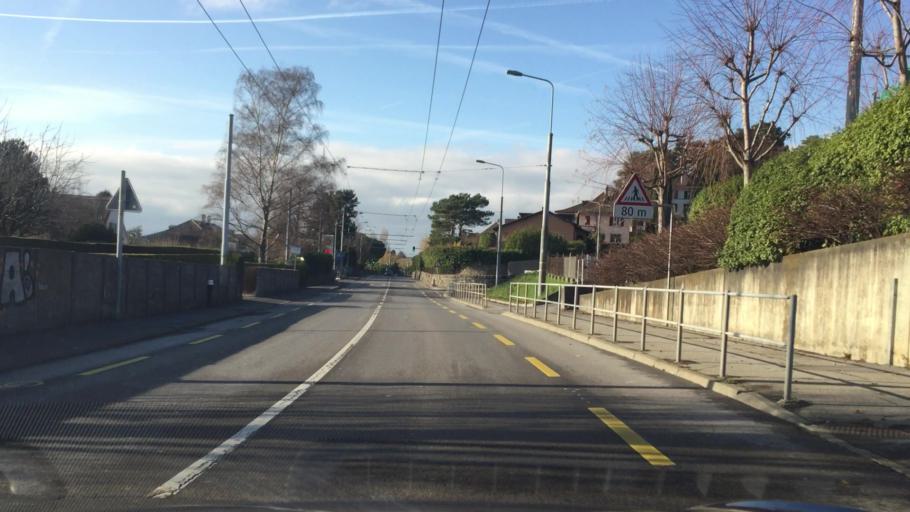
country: CH
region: Vaud
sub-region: Lavaux-Oron District
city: Pully
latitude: 46.5073
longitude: 6.6643
